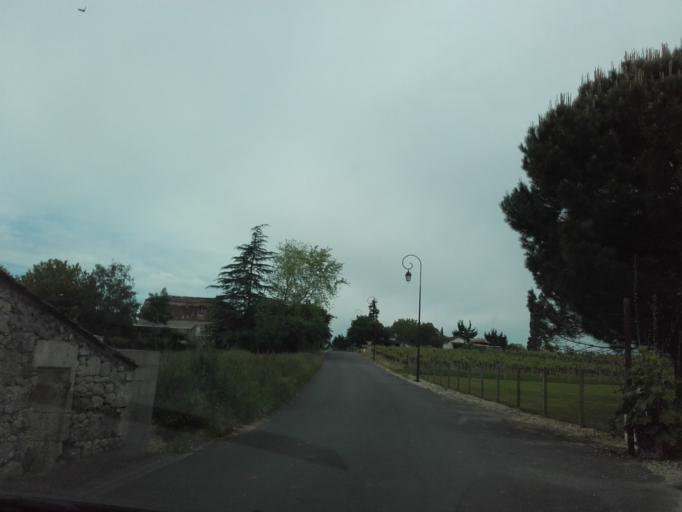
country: FR
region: Aquitaine
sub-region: Departement de la Dordogne
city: Monbazillac
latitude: 44.7819
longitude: 0.4504
